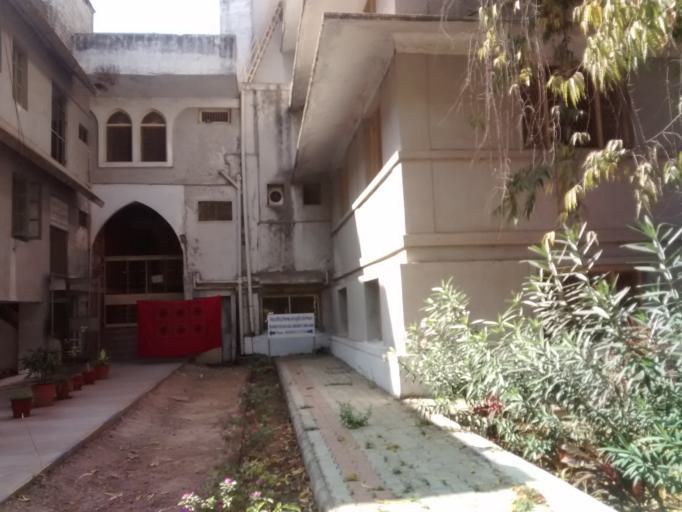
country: IN
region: Gujarat
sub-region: Ahmadabad
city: Ahmedabad
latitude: 23.0436
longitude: 72.5692
